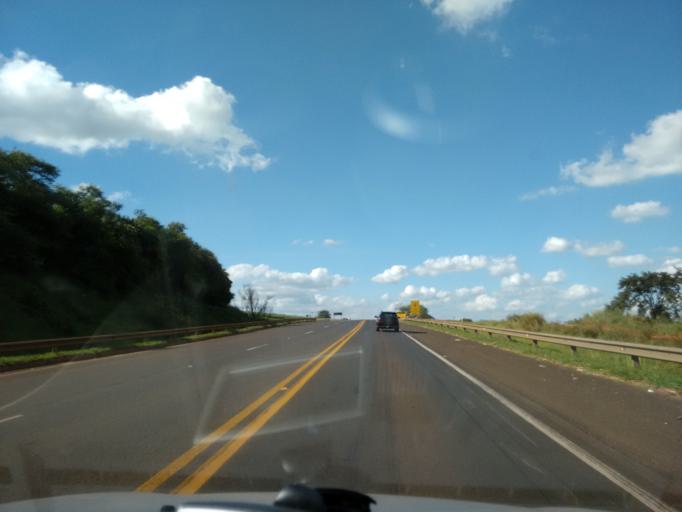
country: BR
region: Sao Paulo
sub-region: Americo Brasiliense
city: Americo Brasiliense
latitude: -21.7566
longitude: -48.0712
